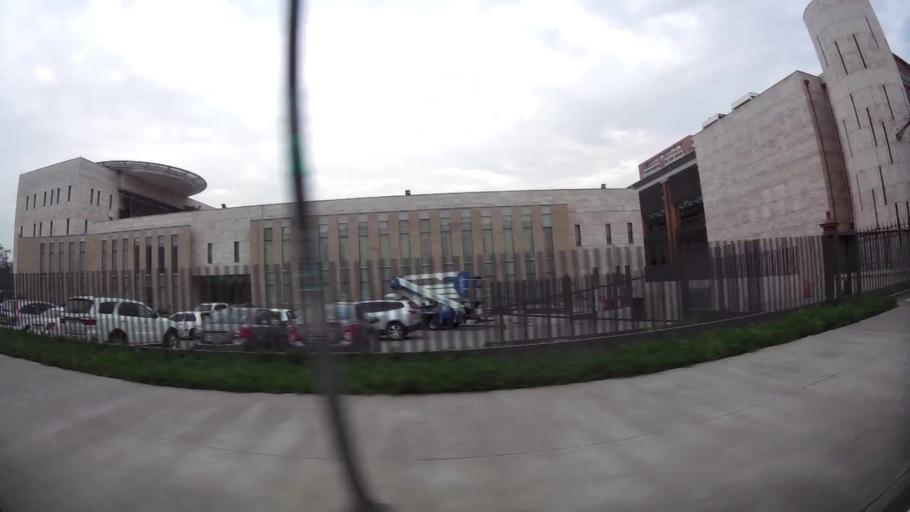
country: CL
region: Santiago Metropolitan
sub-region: Provincia de Santiago
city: Santiago
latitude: -33.4575
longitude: -70.6570
